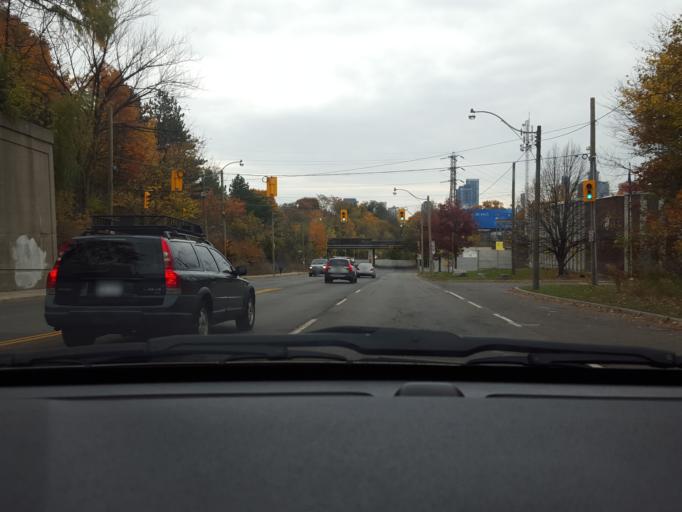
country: CA
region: Ontario
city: Toronto
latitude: 43.6859
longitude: -79.3843
